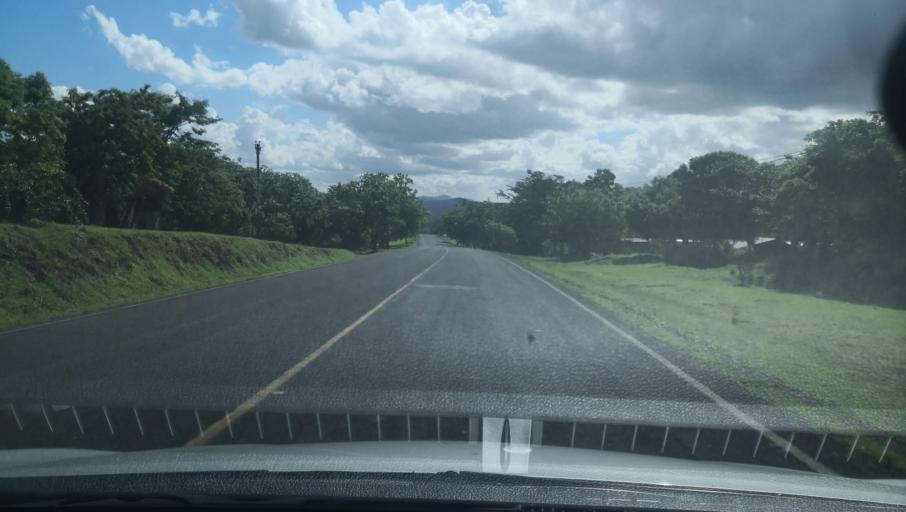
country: NI
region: Madriz
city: Somoto
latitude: 13.4724
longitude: -86.6147
